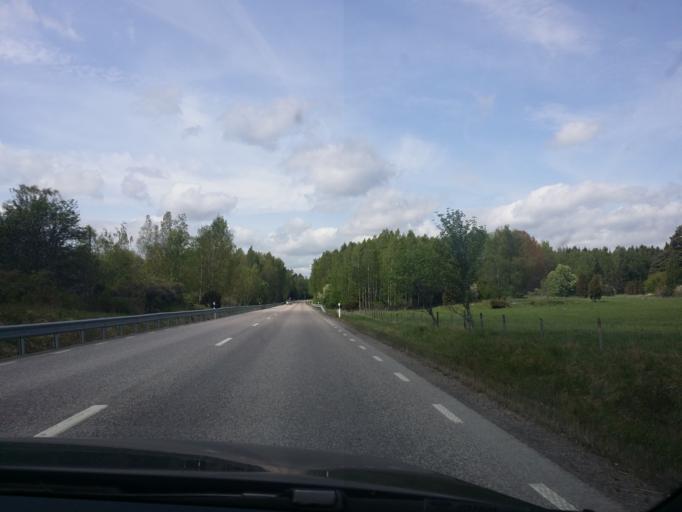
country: SE
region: Uppsala
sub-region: Habo Kommun
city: Balsta
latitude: 59.6327
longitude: 17.5926
